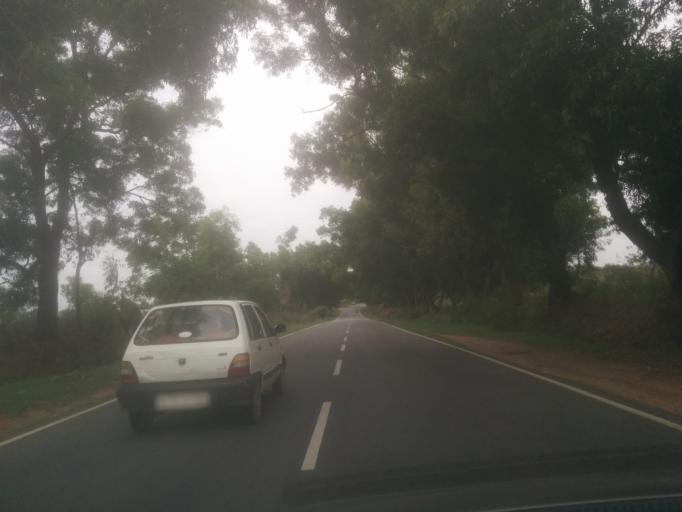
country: IN
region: Karnataka
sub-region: Hassan
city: Belur
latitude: 13.1605
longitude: 75.9019
